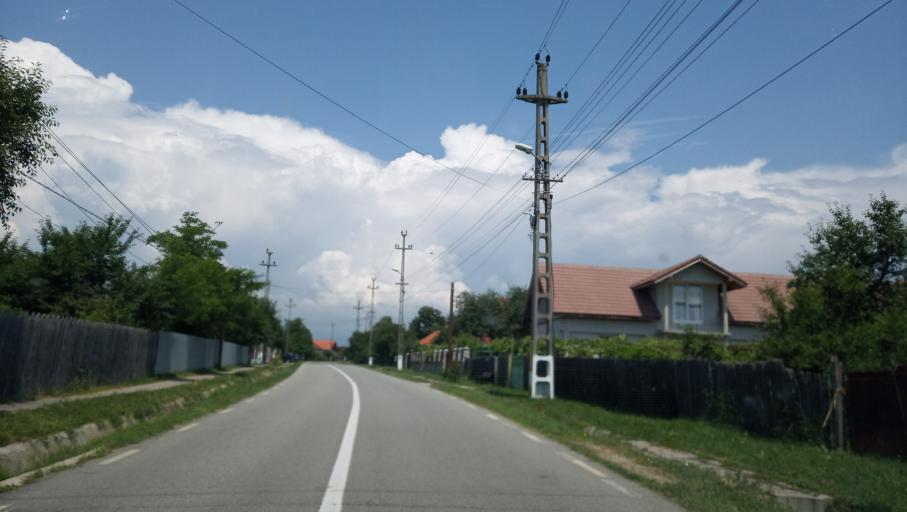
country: RO
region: Gorj
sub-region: Comuna Turcinesti
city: Turcinesti
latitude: 45.0642
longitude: 23.3481
